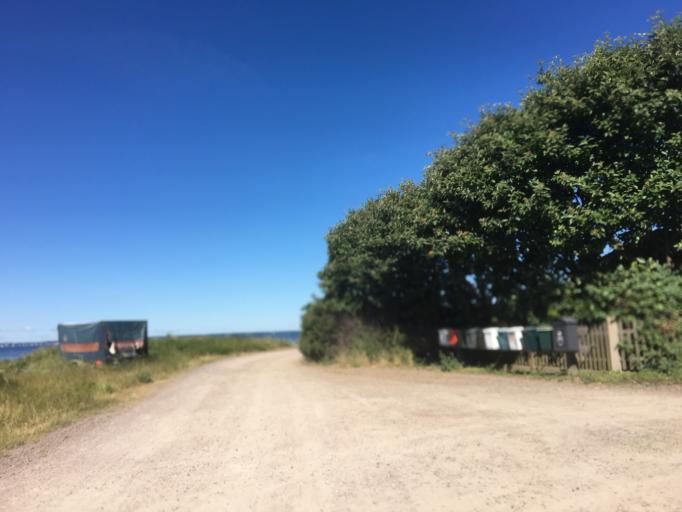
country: SE
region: Skane
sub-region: Helsingborg
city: Rydeback
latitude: 55.9117
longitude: 12.6723
